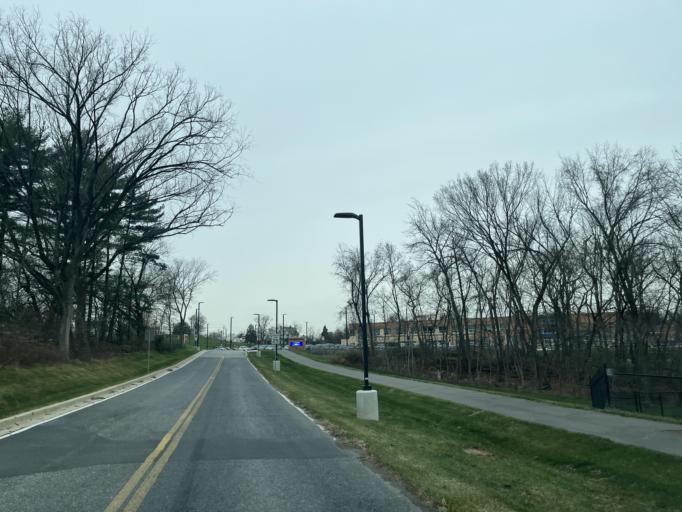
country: US
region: Maryland
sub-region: Anne Arundel County
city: Jessup
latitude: 39.1447
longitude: -76.7654
